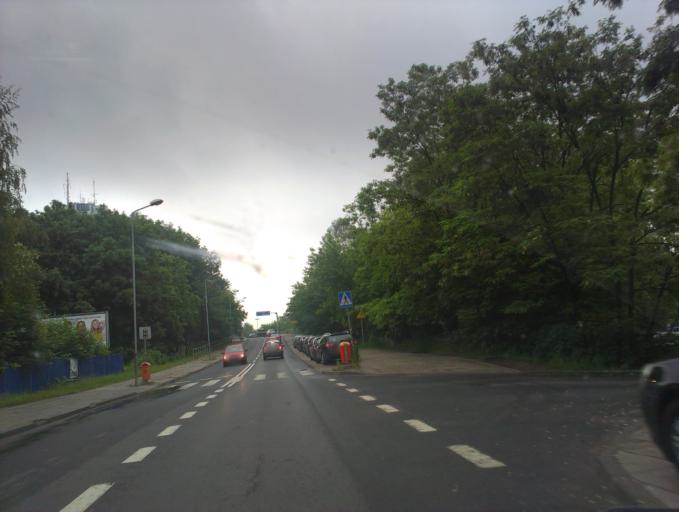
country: PL
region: Silesian Voivodeship
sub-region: Katowice
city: Katowice
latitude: 50.2447
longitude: 19.0147
